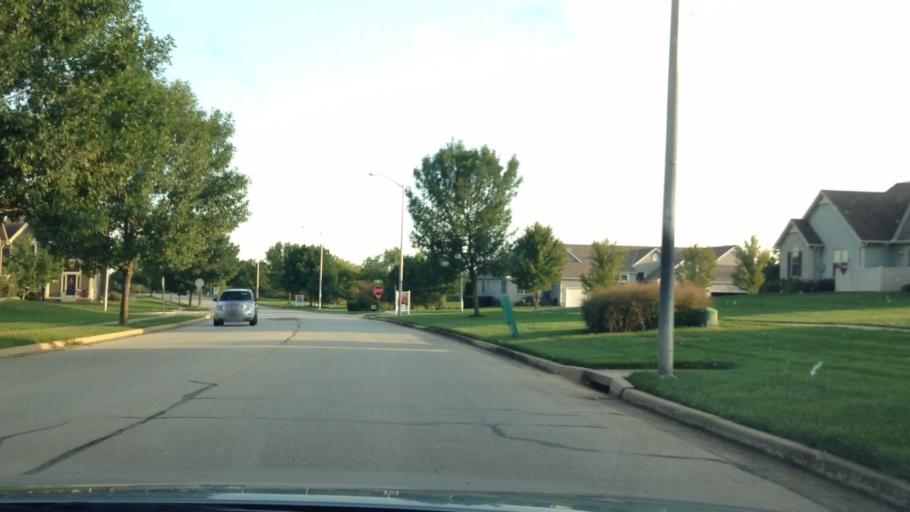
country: US
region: Missouri
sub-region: Clay County
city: Pleasant Valley
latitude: 39.2710
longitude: -94.4846
